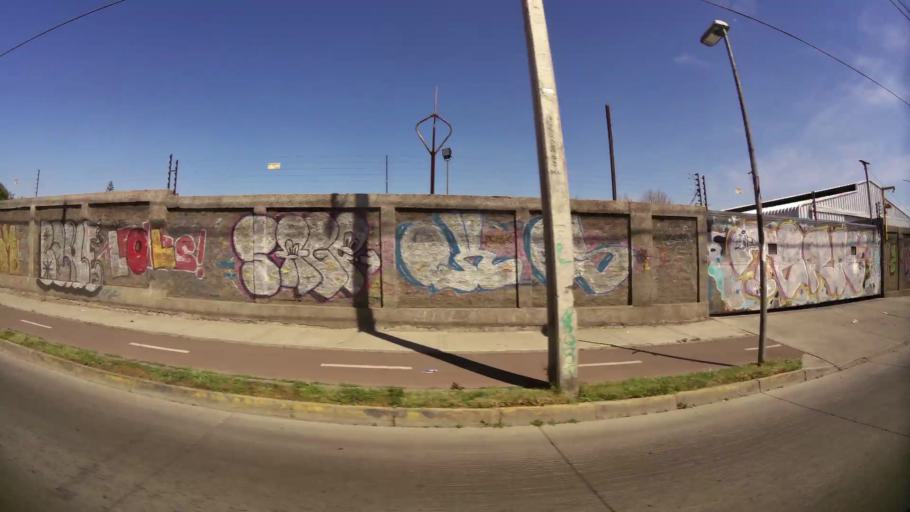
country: CL
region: Santiago Metropolitan
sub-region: Provincia de Santiago
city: Lo Prado
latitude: -33.5111
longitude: -70.7366
